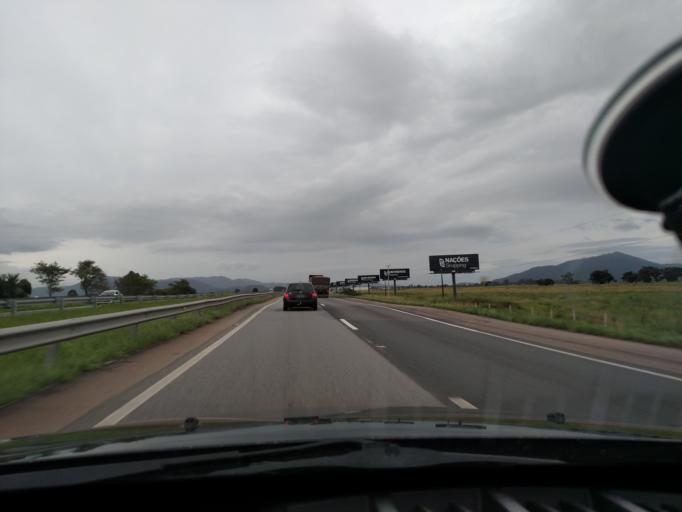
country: BR
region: Santa Catarina
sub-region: Tijucas
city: Tijucas
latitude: -27.2741
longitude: -48.6314
